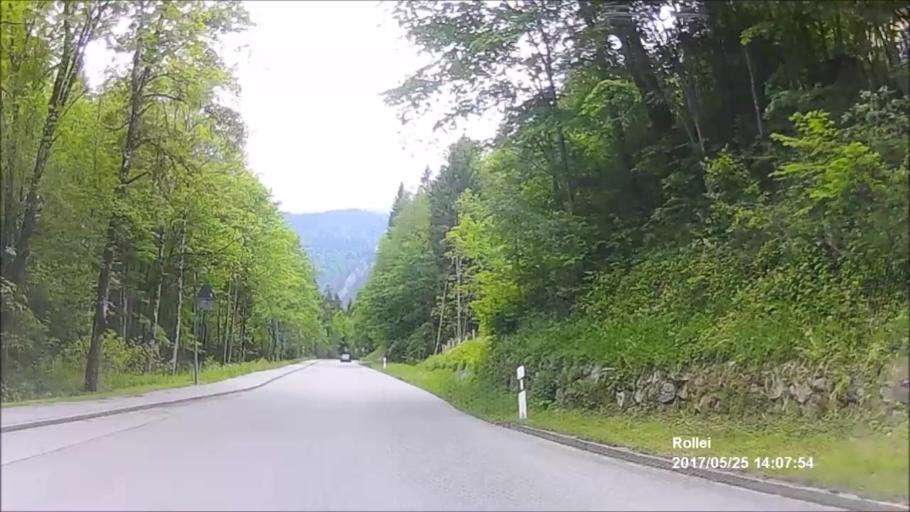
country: DE
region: Bavaria
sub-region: Upper Bavaria
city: Berchtesgaden
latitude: 47.6156
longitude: 12.9966
